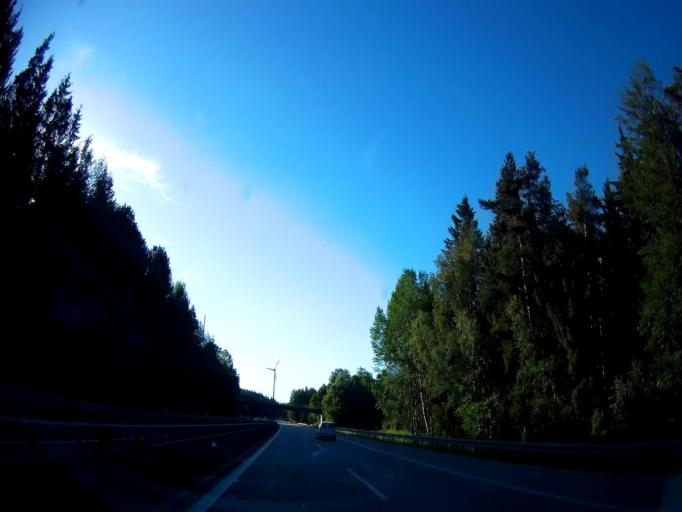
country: DE
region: Bavaria
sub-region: Upper Palatinate
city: Brunn
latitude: 49.1040
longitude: 11.8817
